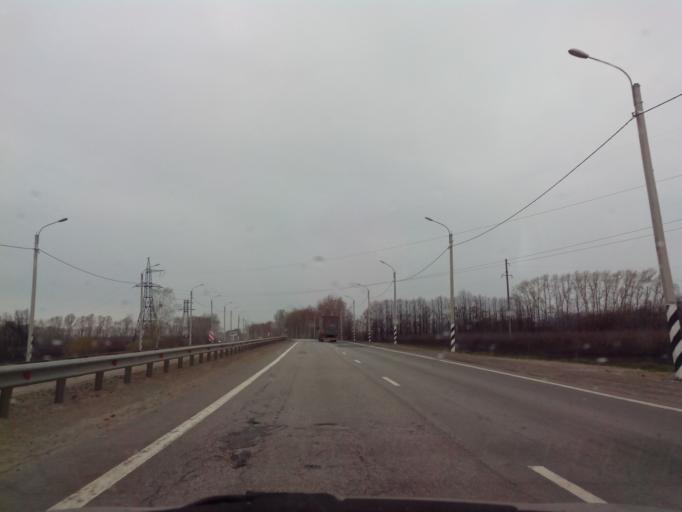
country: RU
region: Tambov
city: Selezni
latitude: 52.7515
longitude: 41.1800
